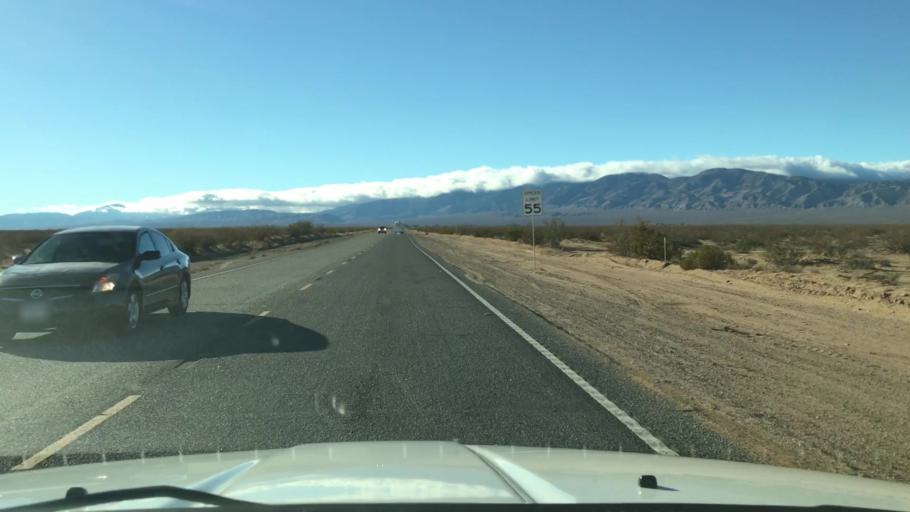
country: US
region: California
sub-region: Kern County
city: California City
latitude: 35.1255
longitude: -118.0498
